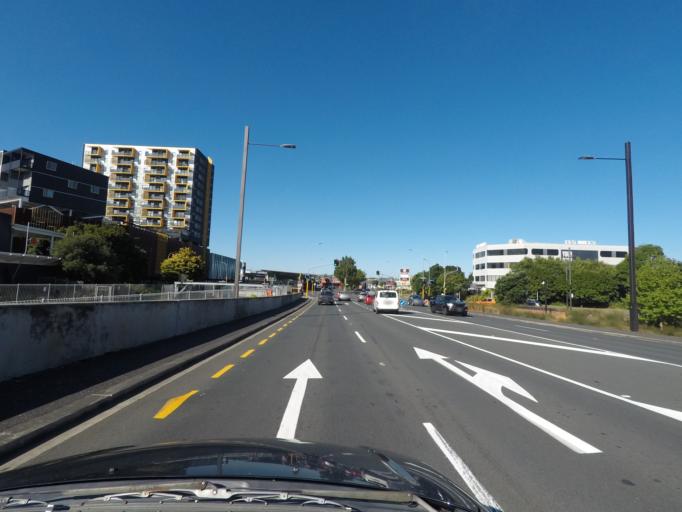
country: NZ
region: Auckland
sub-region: Auckland
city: Waitakere
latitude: -36.9101
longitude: 174.6824
